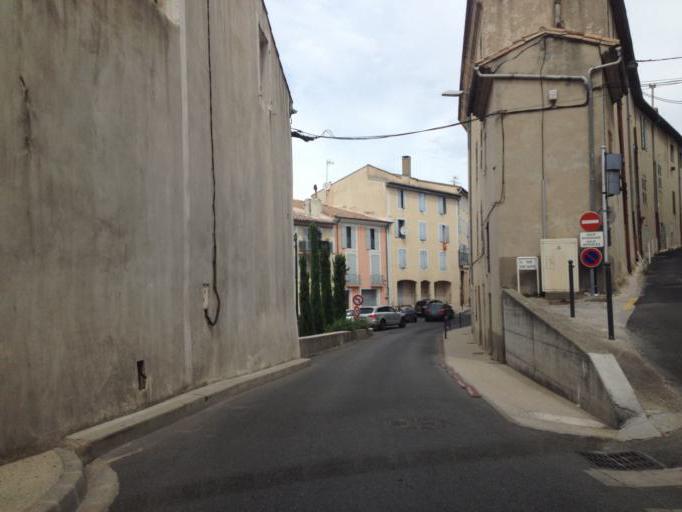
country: FR
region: Rhone-Alpes
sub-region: Departement de la Drome
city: Montelimar
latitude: 44.5589
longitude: 4.7532
